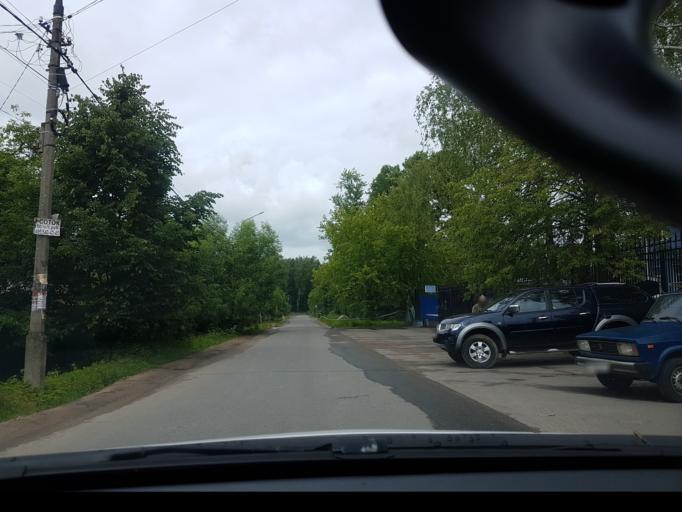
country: RU
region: Moskovskaya
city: Istra
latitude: 55.9245
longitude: 36.8771
